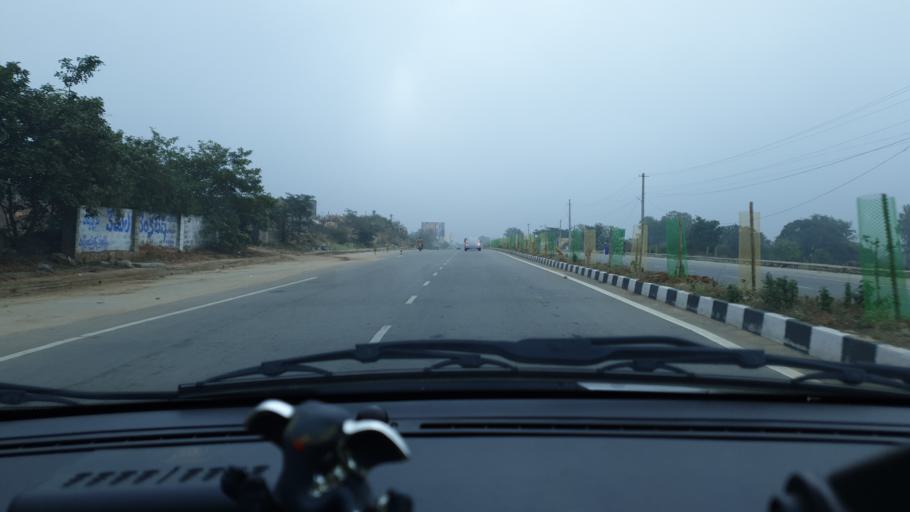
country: IN
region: Telangana
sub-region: Mahbubnagar
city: Farrukhnagar
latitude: 16.9540
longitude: 78.5179
